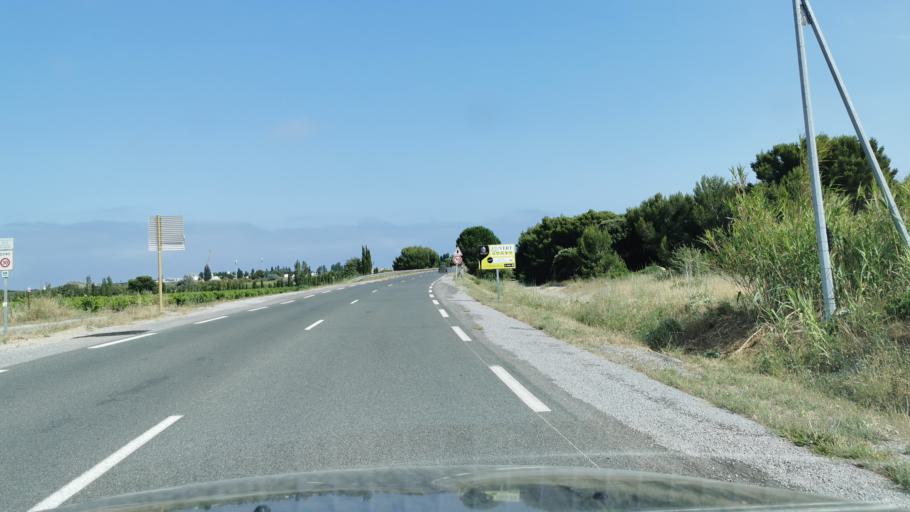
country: FR
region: Languedoc-Roussillon
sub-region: Departement de l'Aude
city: Gruissan
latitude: 43.1207
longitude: 3.1009
